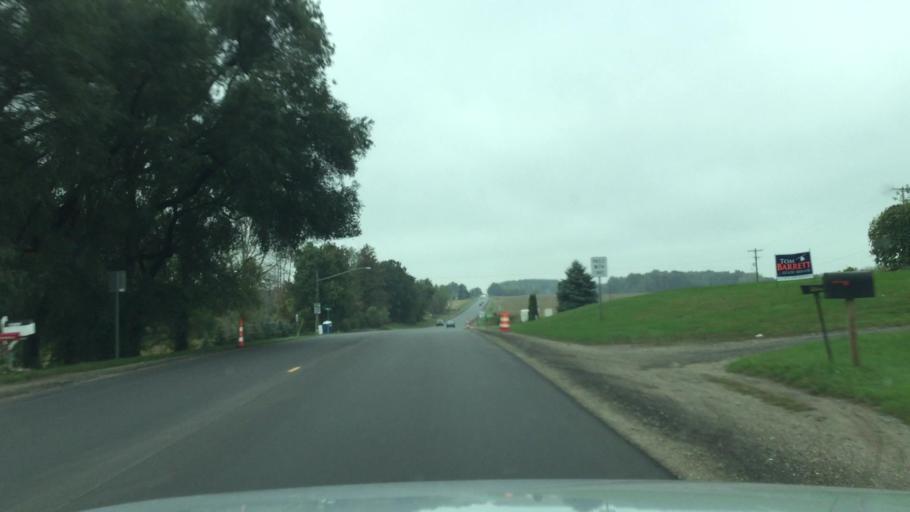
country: US
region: Michigan
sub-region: Shiawassee County
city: Perry
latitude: 42.8646
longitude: -84.2211
